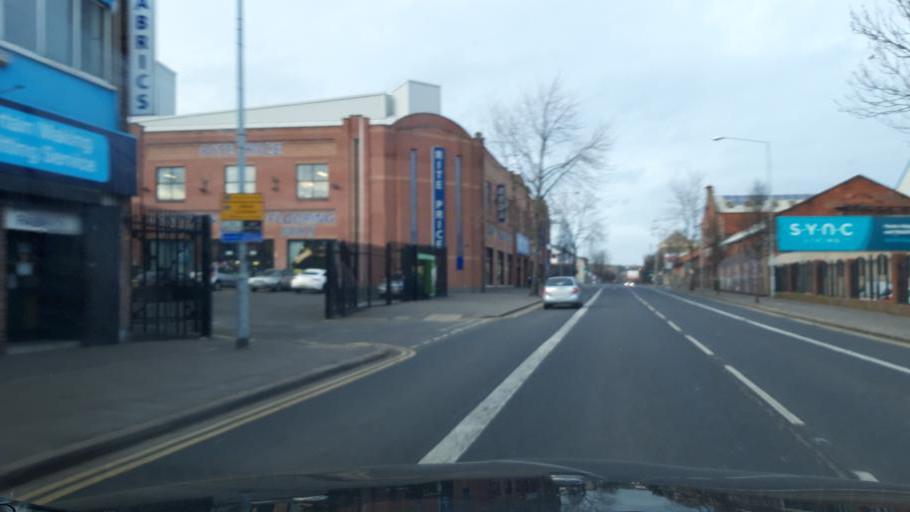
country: GB
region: Northern Ireland
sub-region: City of Belfast
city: Belfast
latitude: 54.6126
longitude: -5.9237
